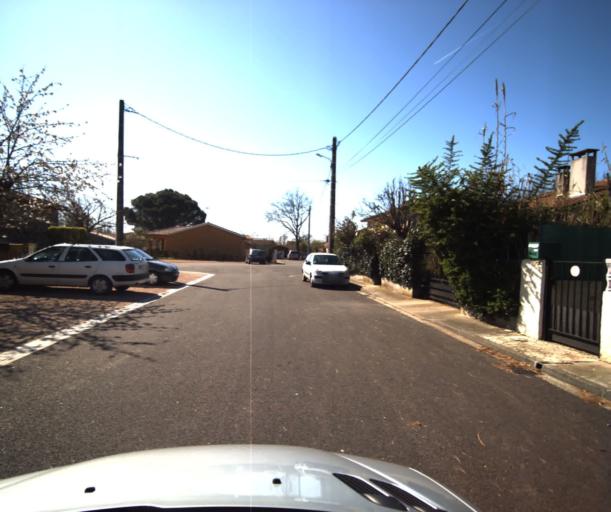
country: FR
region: Midi-Pyrenees
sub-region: Departement du Tarn-et-Garonne
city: Bressols
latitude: 43.9661
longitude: 1.3391
